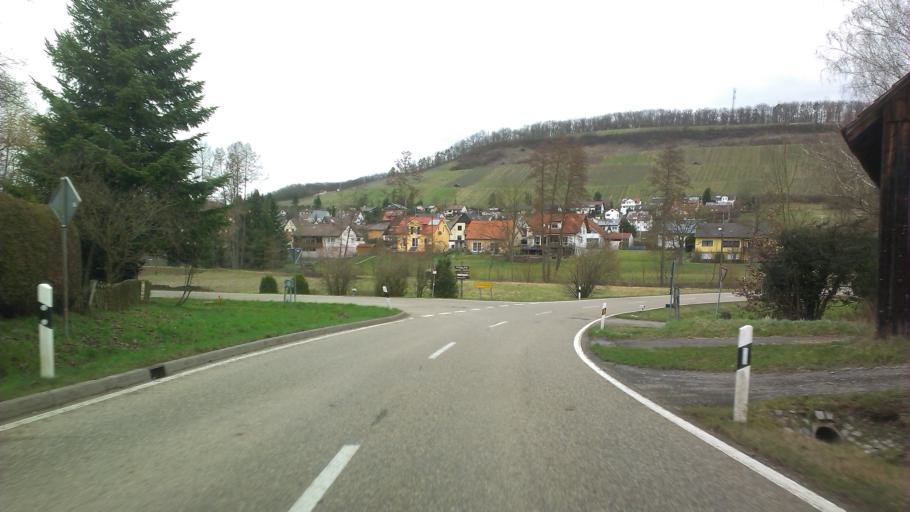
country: DE
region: Baden-Wuerttemberg
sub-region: Karlsruhe Region
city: Illingen
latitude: 48.9924
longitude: 8.9055
